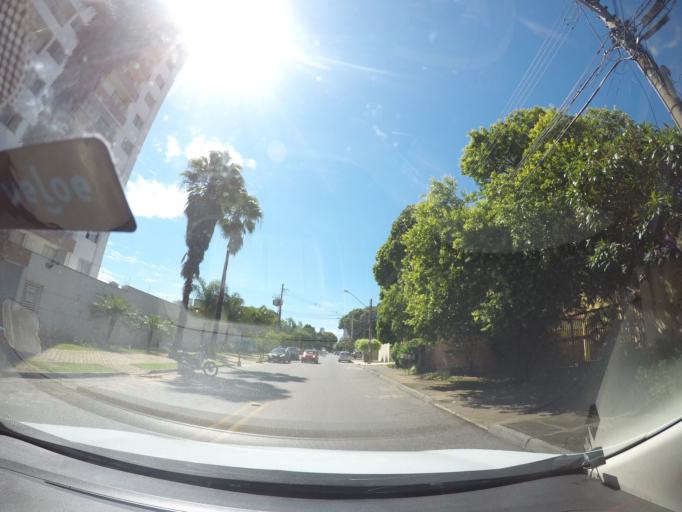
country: BR
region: Goias
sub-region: Goiania
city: Goiania
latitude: -16.6997
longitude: -49.2870
